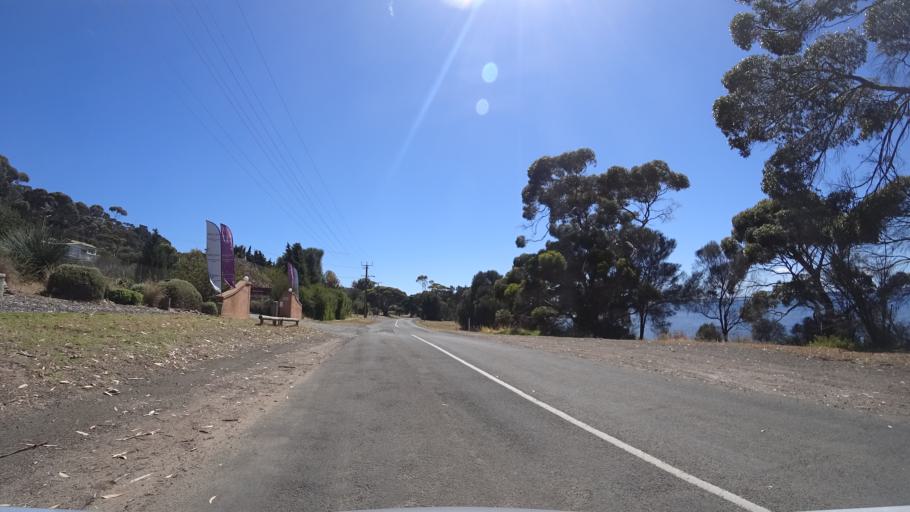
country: AU
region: South Australia
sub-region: Kangaroo Island
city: Kingscote
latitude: -35.7756
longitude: 137.7772
